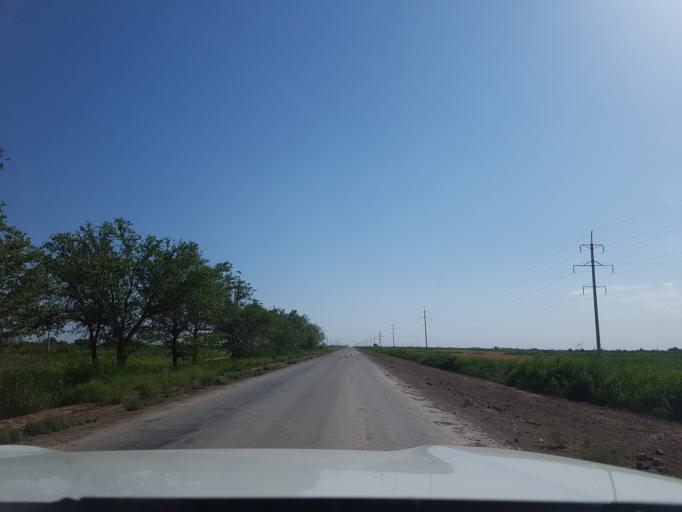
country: TM
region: Dasoguz
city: Koeneuergench
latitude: 42.1053
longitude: 58.9094
